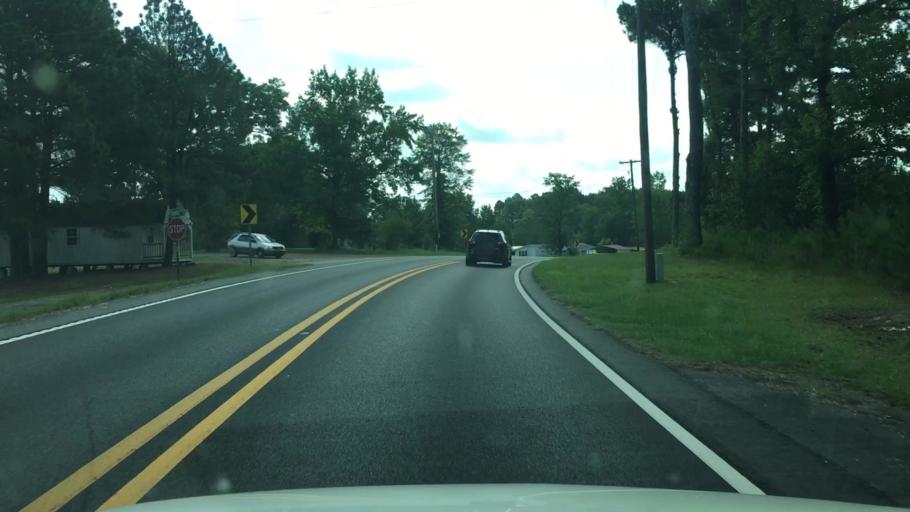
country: US
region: Arkansas
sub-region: Garland County
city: Lake Hamilton
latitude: 34.2779
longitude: -93.1526
